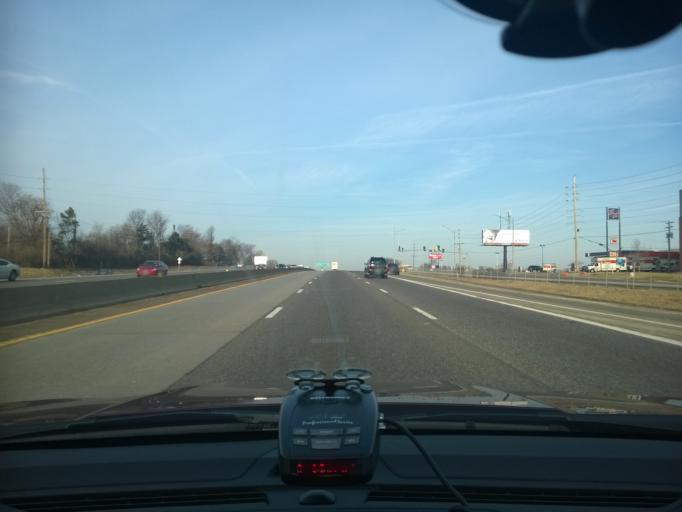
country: US
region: Missouri
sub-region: Saint Charles County
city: Saint Charles
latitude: 38.7873
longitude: -90.5361
